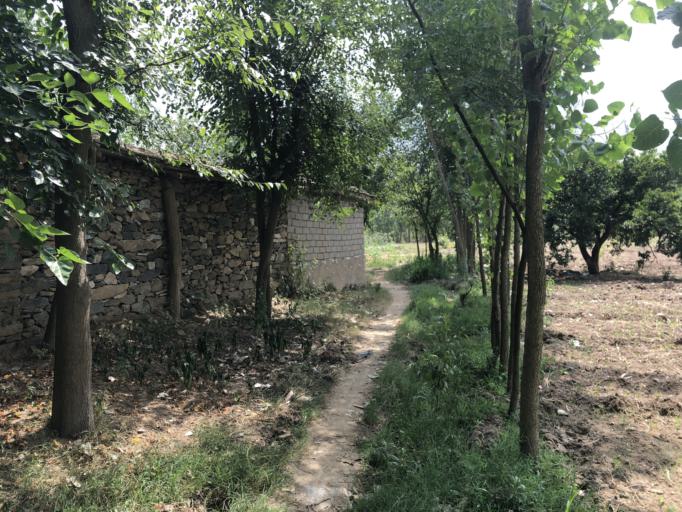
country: PK
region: Khyber Pakhtunkhwa
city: Daggar
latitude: 34.5451
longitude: 72.3590
